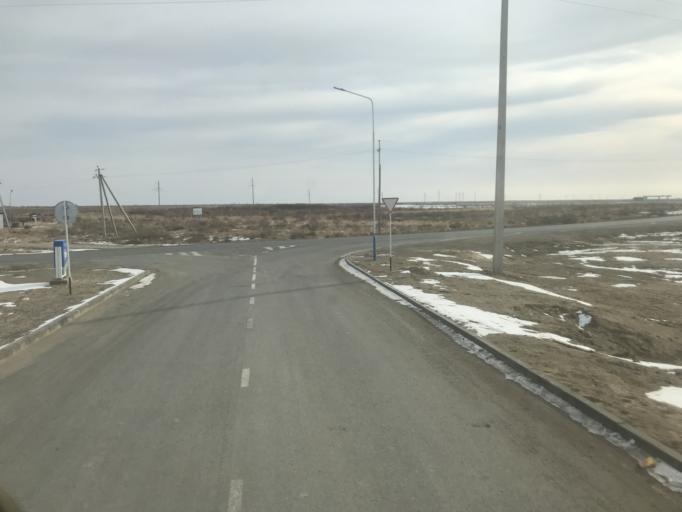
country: KZ
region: Qyzylorda
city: Ayteke Bi
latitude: 45.8757
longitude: 62.1490
